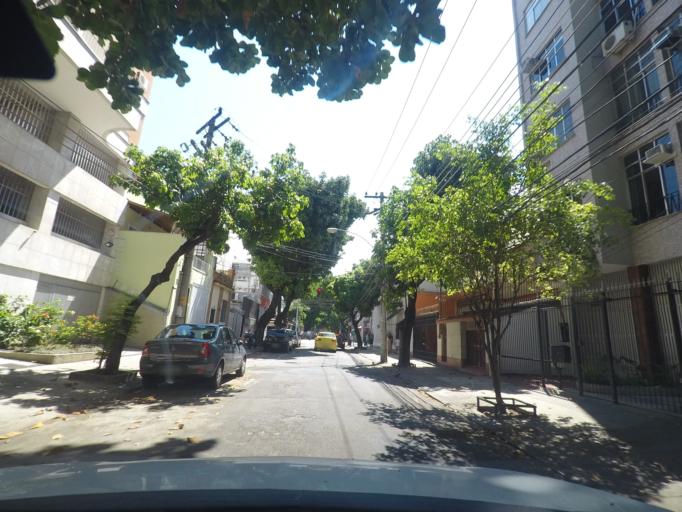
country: BR
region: Rio de Janeiro
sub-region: Rio De Janeiro
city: Rio de Janeiro
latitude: -22.9218
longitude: -43.2364
